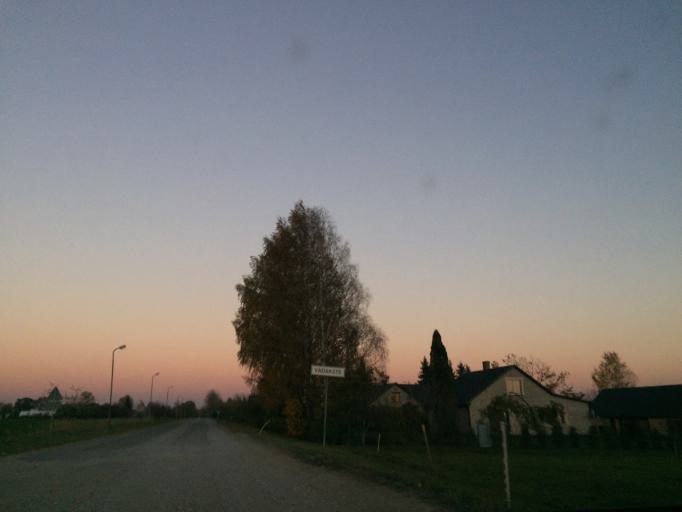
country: LT
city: Akmene
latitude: 56.3764
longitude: 22.7365
